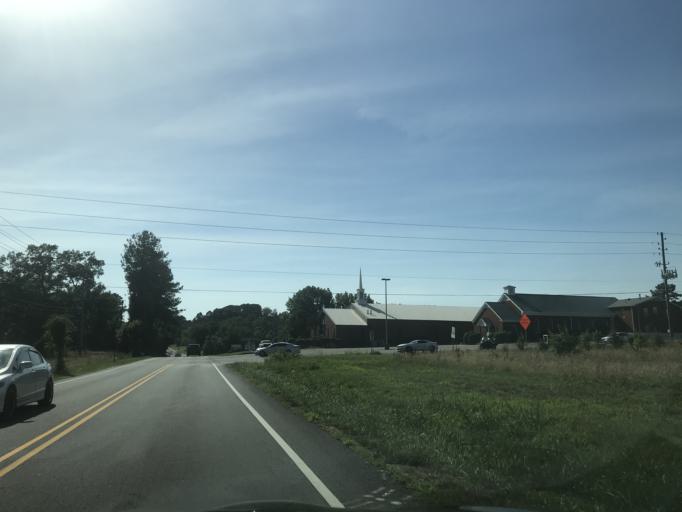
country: US
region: North Carolina
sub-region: Wake County
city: Garner
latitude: 35.6611
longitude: -78.5464
